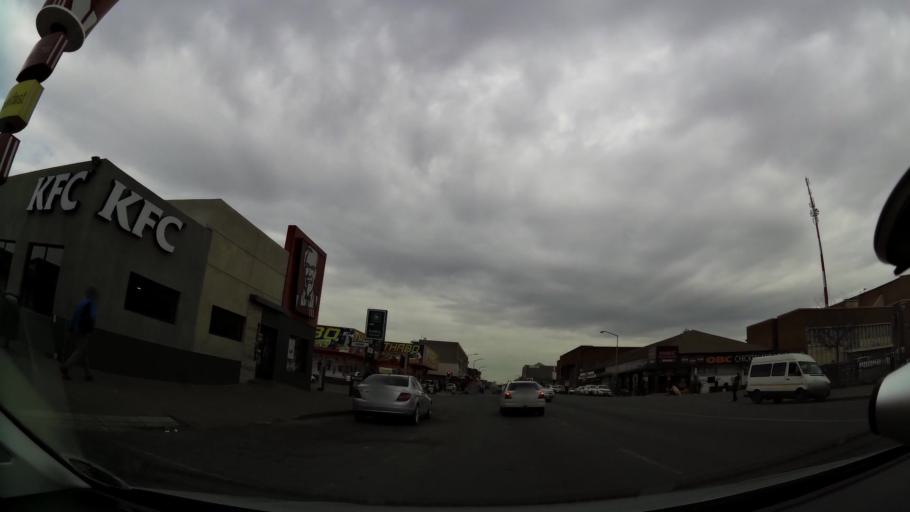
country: ZA
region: Orange Free State
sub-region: Fezile Dabi District Municipality
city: Kroonstad
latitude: -27.6616
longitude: 27.2358
